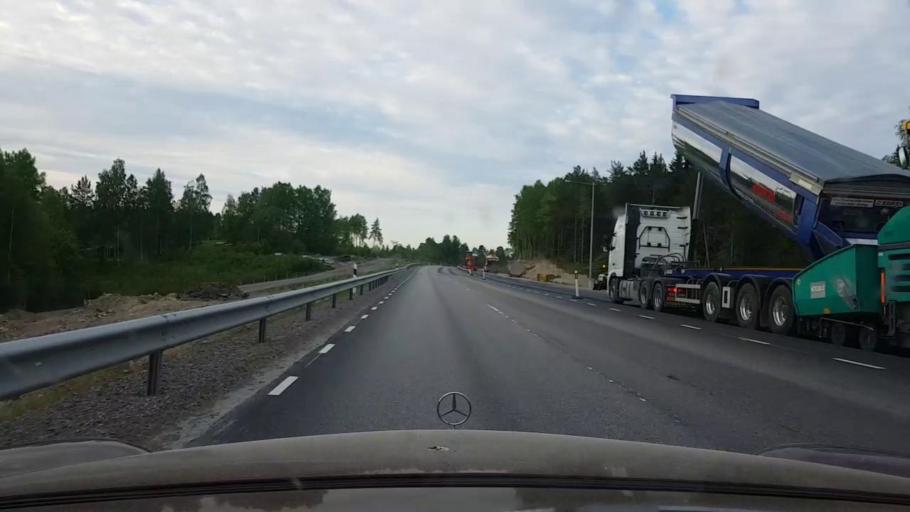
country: SE
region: OErebro
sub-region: Askersunds Kommun
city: Askersund
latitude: 58.9158
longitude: 14.9781
